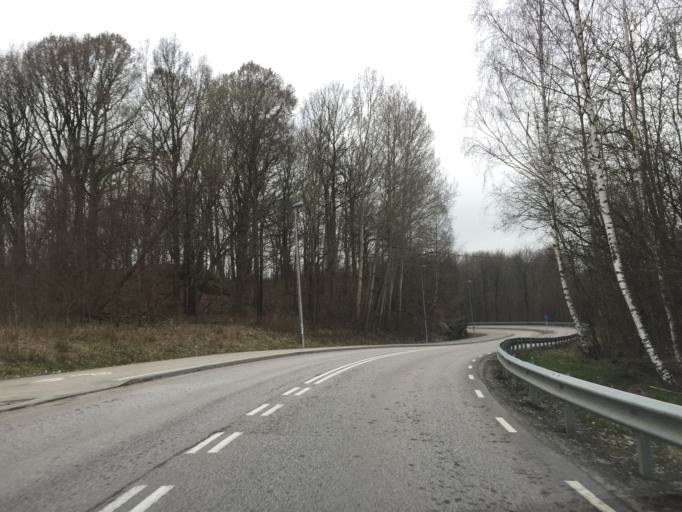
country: SE
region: Vaestra Goetaland
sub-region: Goteborg
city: Eriksbo
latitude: 57.7596
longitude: 12.0145
